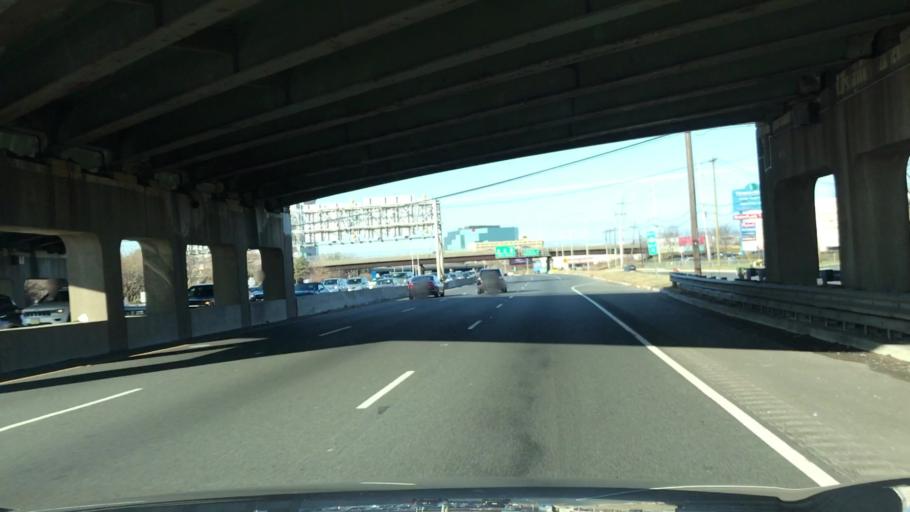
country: US
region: New Jersey
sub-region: Hudson County
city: Secaucus
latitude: 40.7834
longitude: -74.0473
